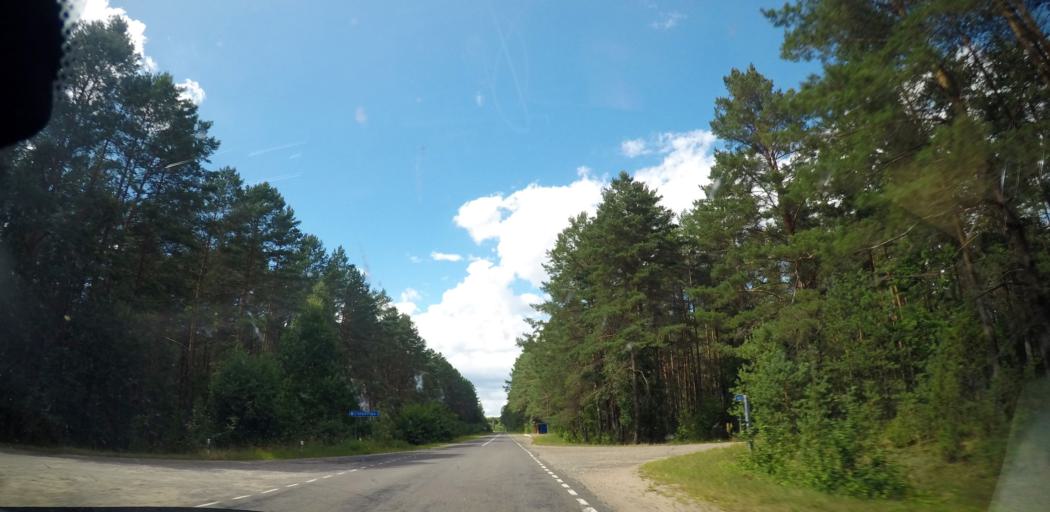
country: LT
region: Alytaus apskritis
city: Druskininkai
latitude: 53.8670
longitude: 24.1674
